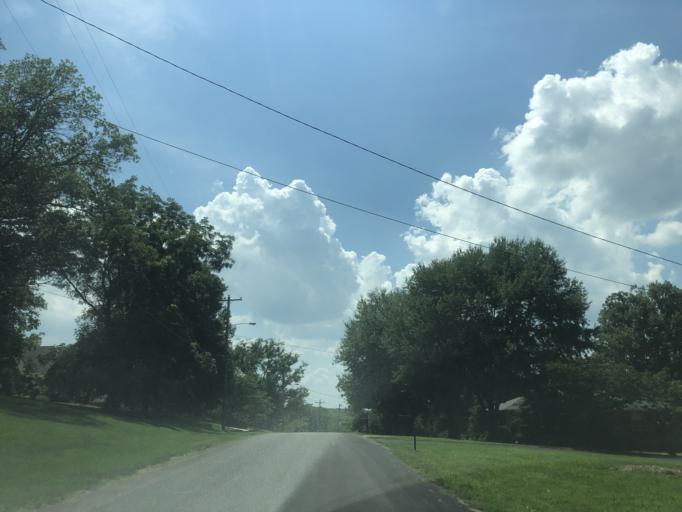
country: US
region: Tennessee
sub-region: Davidson County
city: Lakewood
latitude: 36.1788
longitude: -86.6695
